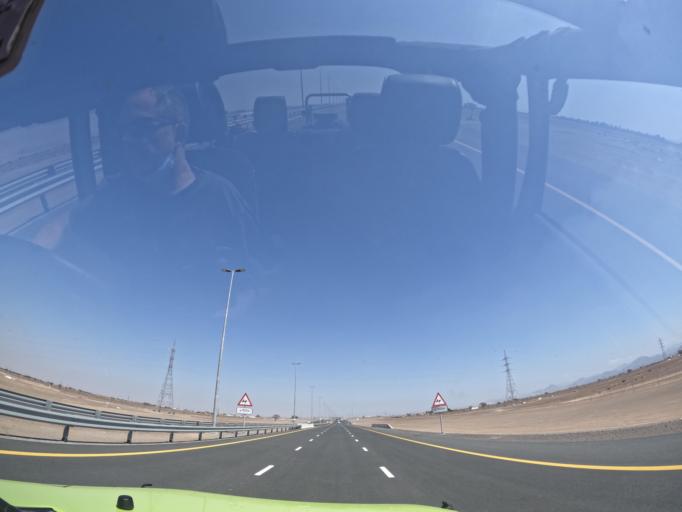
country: AE
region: Ash Shariqah
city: Adh Dhayd
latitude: 25.1004
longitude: 55.9277
